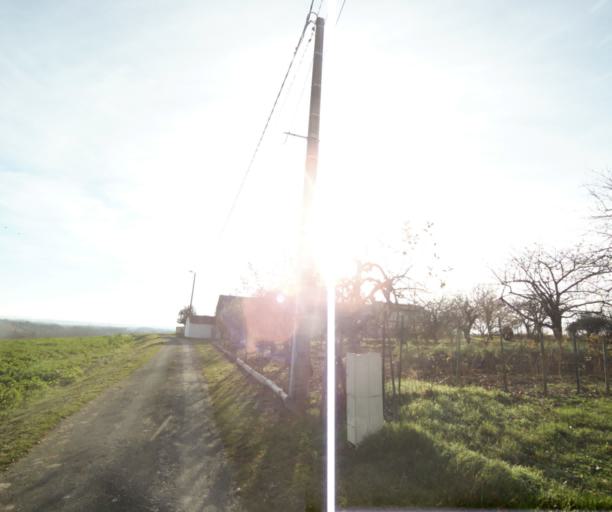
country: FR
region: Poitou-Charentes
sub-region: Departement de la Charente-Maritime
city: Chaniers
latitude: 45.7228
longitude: -0.5239
